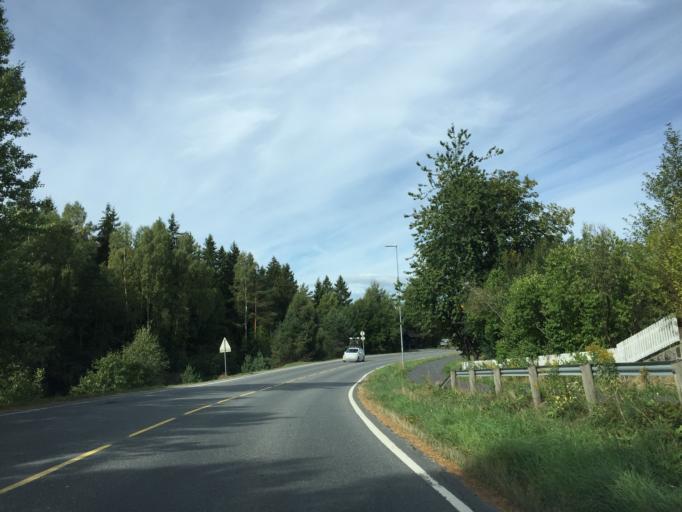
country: NO
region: Ostfold
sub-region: Moss
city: Moss
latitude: 59.5184
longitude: 10.7048
